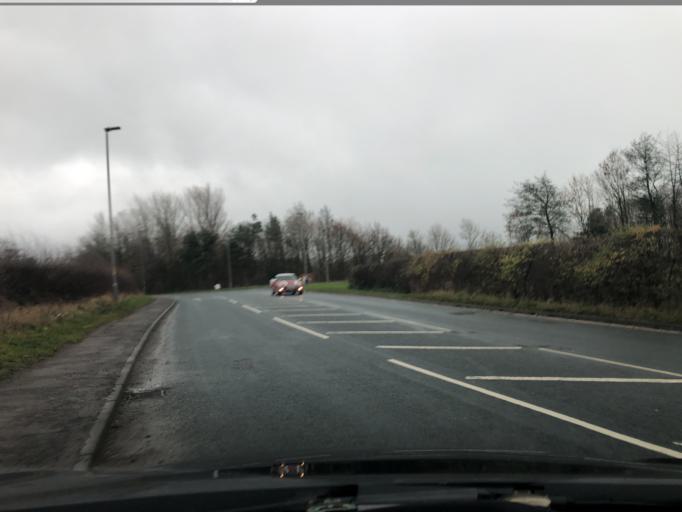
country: GB
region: England
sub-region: North Yorkshire
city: Stokesley
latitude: 54.4657
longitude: -1.1731
